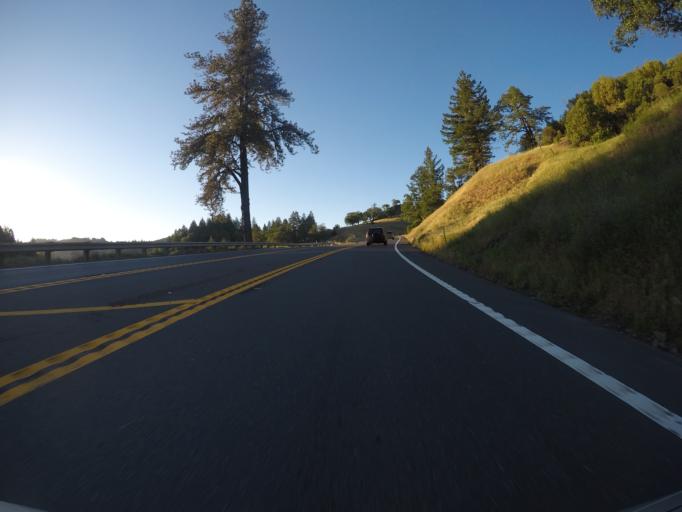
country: US
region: California
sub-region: Mendocino County
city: Laytonville
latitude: 39.7693
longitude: -123.5453
